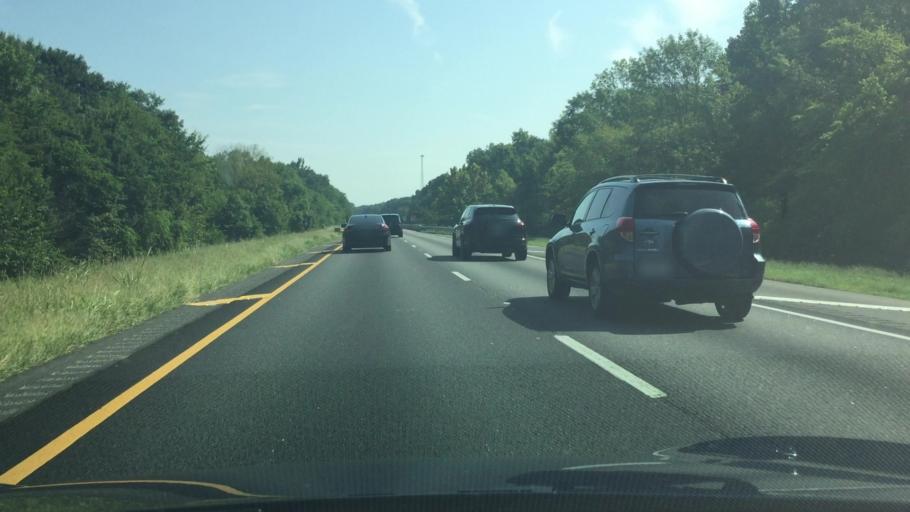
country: US
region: Alabama
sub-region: Montgomery County
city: Montgomery
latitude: 32.2256
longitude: -86.3904
